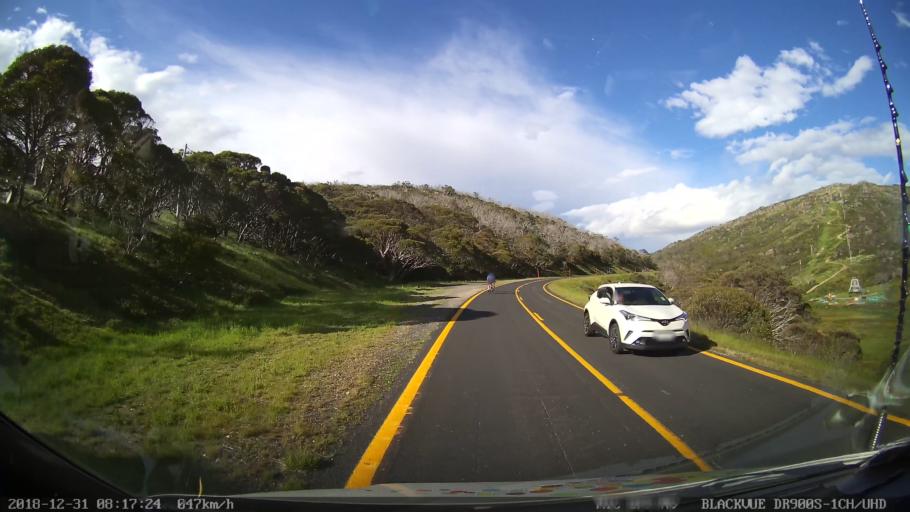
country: AU
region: New South Wales
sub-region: Snowy River
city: Jindabyne
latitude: -36.4104
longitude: 148.4048
